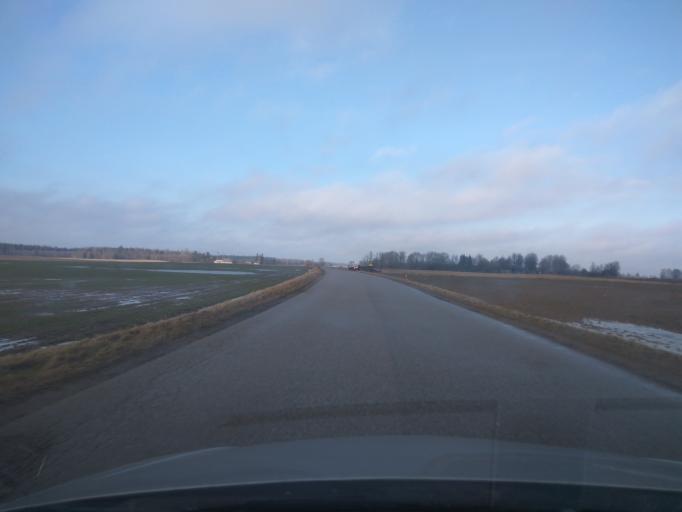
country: LV
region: Saldus Rajons
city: Saldus
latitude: 56.7942
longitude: 22.3847
